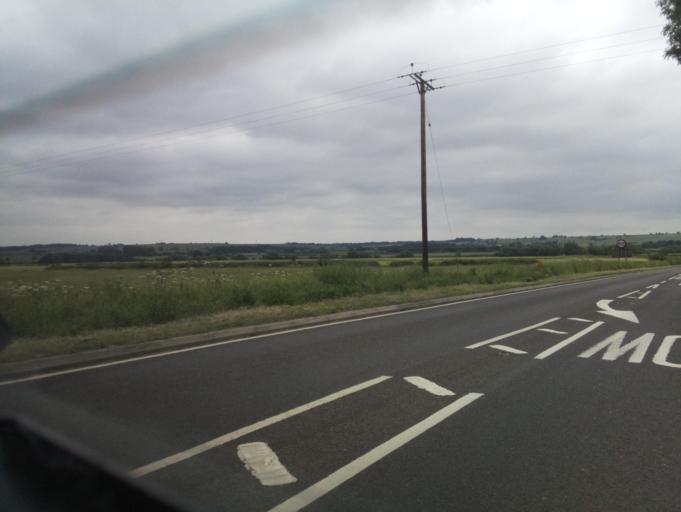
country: GB
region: England
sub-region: Leicestershire
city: Melton Mowbray
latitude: 52.7418
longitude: -0.8618
